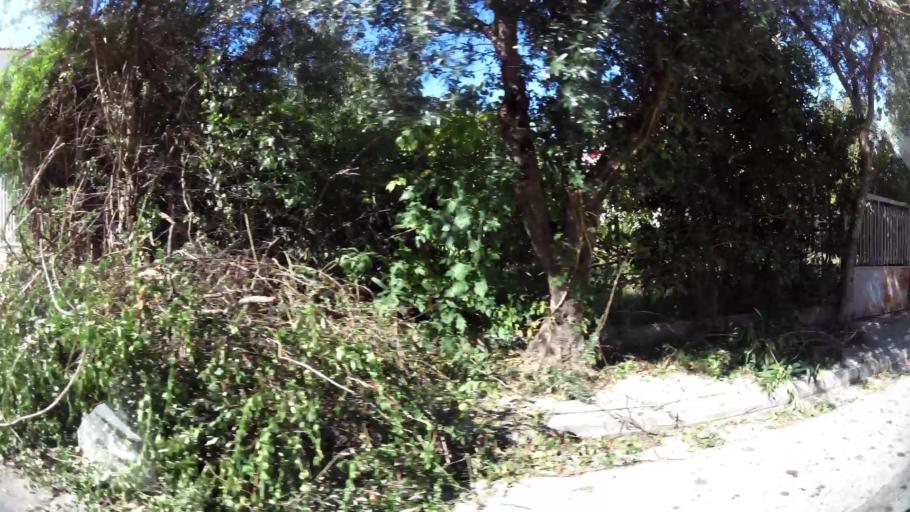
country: GR
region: Attica
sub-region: Nomarchia Anatolikis Attikis
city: Leondarion
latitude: 37.9881
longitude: 23.8548
